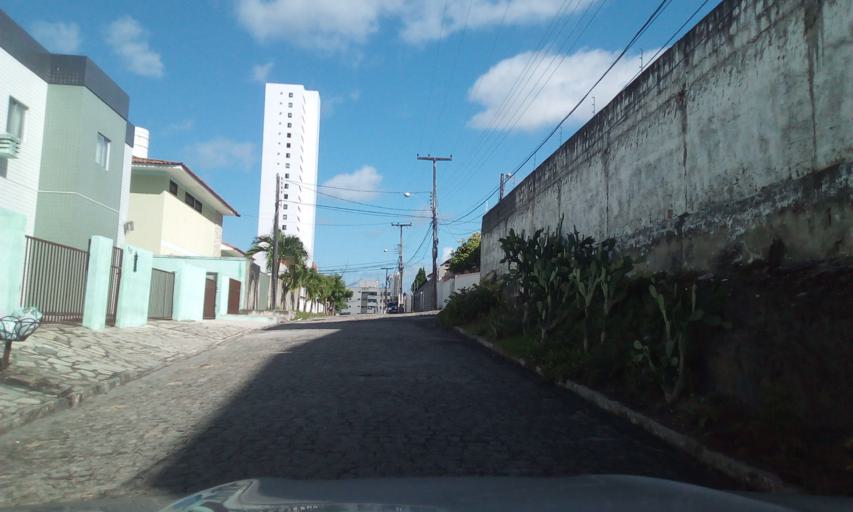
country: BR
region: Paraiba
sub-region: Joao Pessoa
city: Joao Pessoa
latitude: -7.1111
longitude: -34.8468
